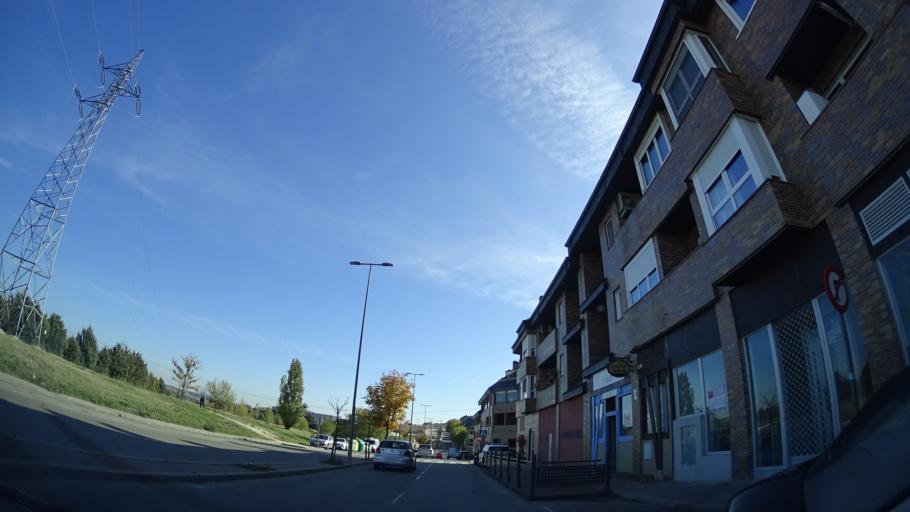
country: ES
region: Madrid
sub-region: Provincia de Madrid
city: Villanueva del Pardillo
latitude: 40.4920
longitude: -3.9579
